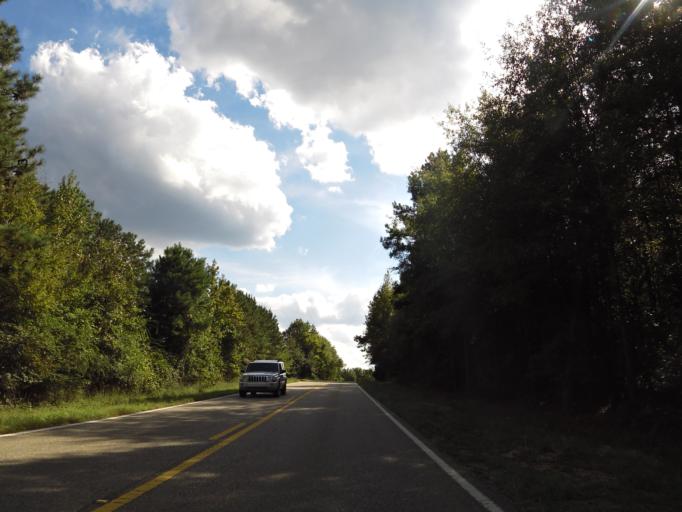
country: US
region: Alabama
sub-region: Dallas County
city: Selmont-West Selmont
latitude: 32.1475
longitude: -87.0741
